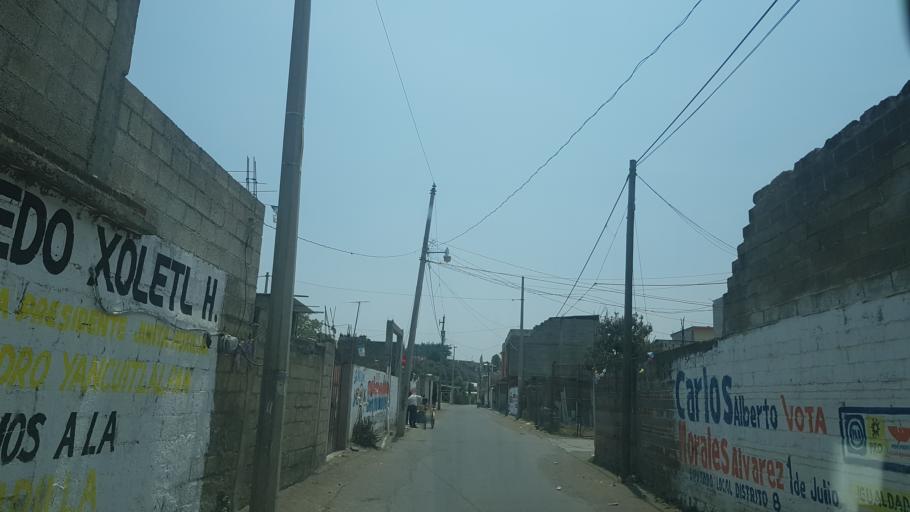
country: MX
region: Puebla
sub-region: San Nicolas de los Ranchos
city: San Pedro Yancuitlalpan
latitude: 19.0782
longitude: -98.4830
